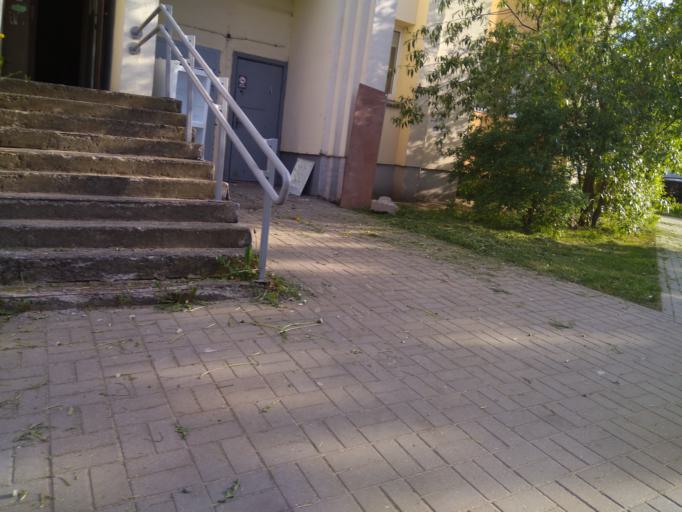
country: BY
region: Minsk
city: Minsk
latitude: 53.9111
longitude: 27.5328
